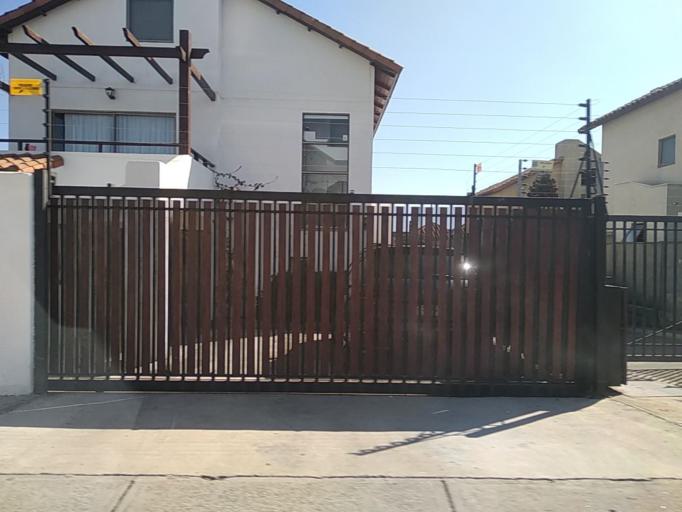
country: CL
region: Valparaiso
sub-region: Provincia de Valparaiso
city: Vina del Mar
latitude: -32.9409
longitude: -71.5440
